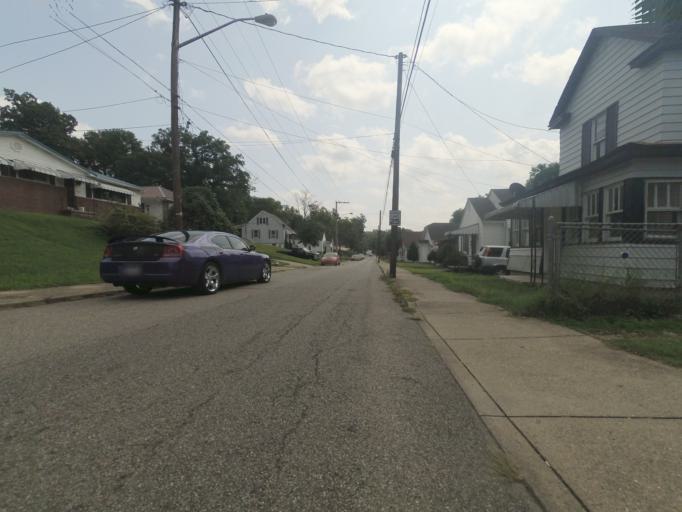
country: US
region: West Virginia
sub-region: Cabell County
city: Huntington
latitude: 38.4122
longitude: -82.4009
